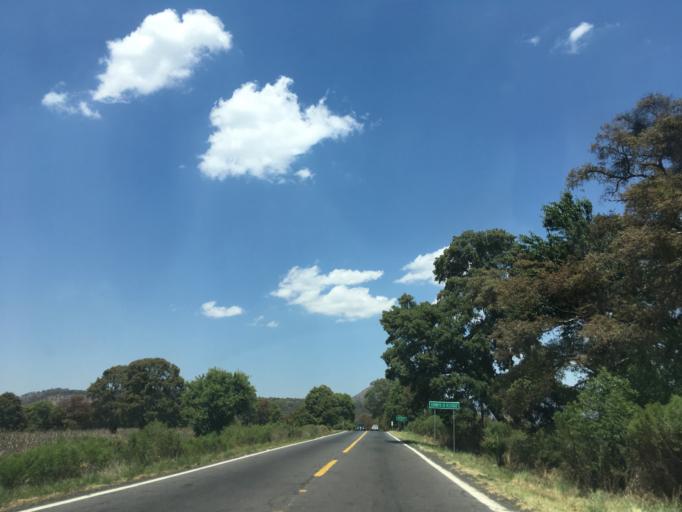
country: MX
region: Mexico
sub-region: Chalco
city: Zopoco
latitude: 19.7940
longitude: -102.0256
